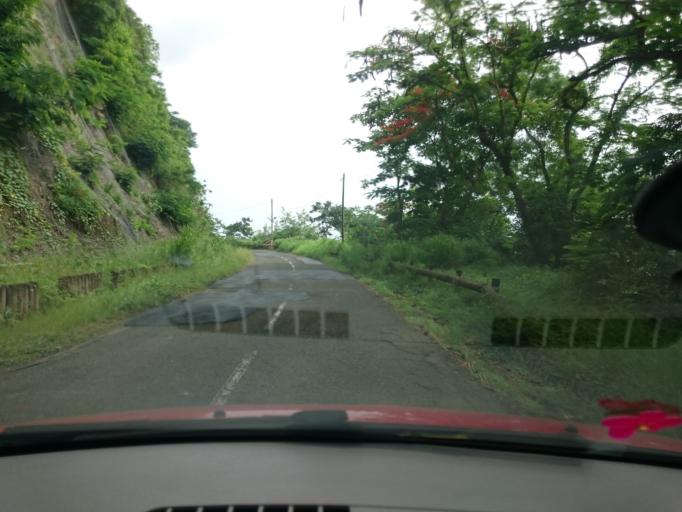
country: MQ
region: Martinique
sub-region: Martinique
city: Saint-Pierre
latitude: 14.8268
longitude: -61.2269
